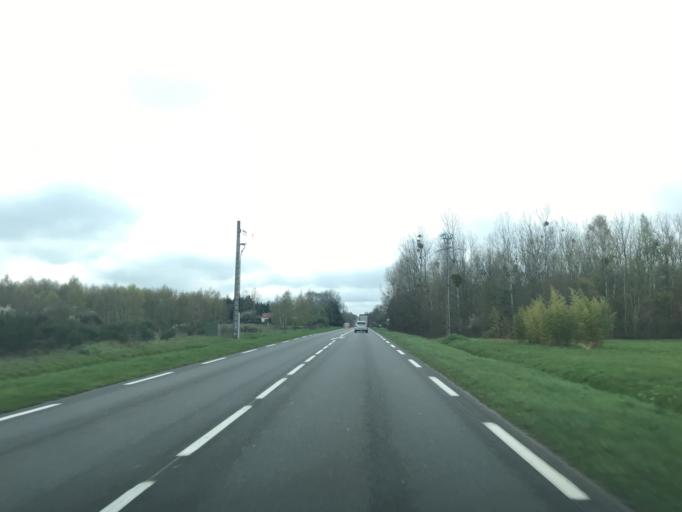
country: FR
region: Centre
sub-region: Departement du Loiret
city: Saint-Benoit-sur-Loire
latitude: 47.8490
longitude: 2.3016
